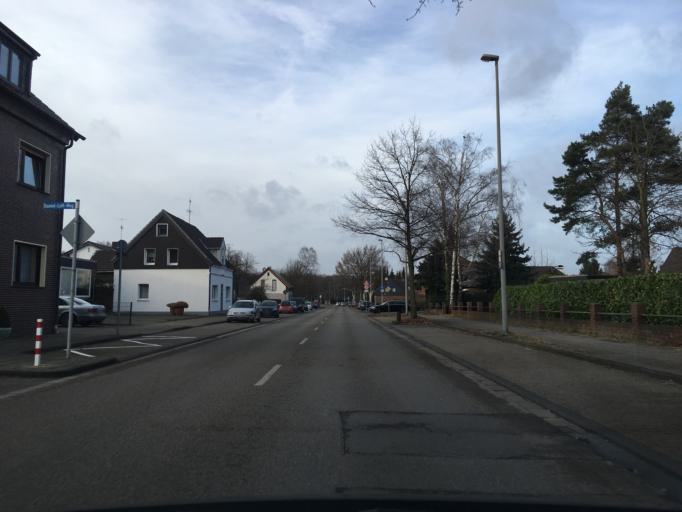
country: DE
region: North Rhine-Westphalia
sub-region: Regierungsbezirk Dusseldorf
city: Oberhausen
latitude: 51.5545
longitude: 6.8432
